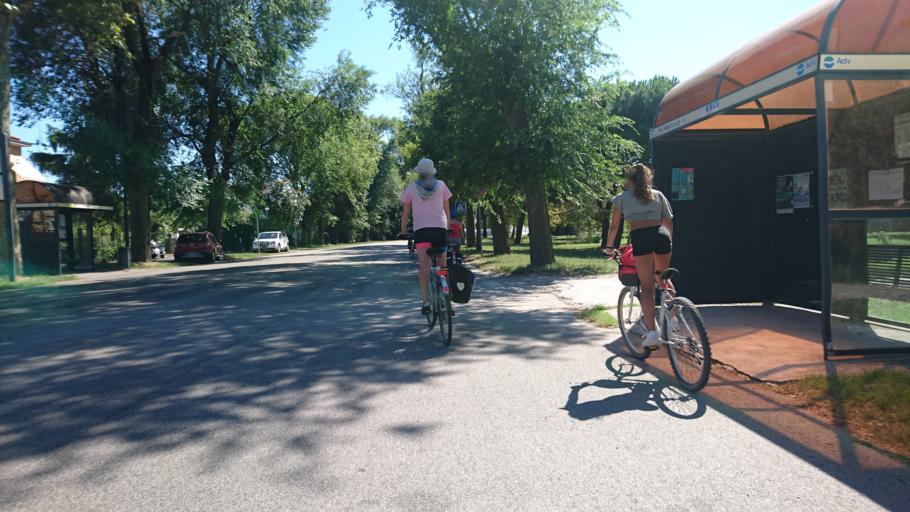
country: IT
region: Veneto
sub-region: Provincia di Venezia
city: Lido
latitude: 45.3744
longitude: 12.3386
